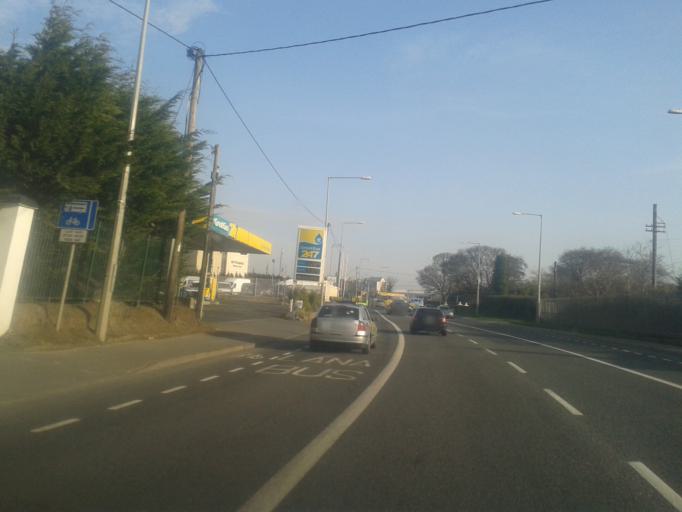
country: IE
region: Leinster
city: Beaumont
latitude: 53.4140
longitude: -6.2390
